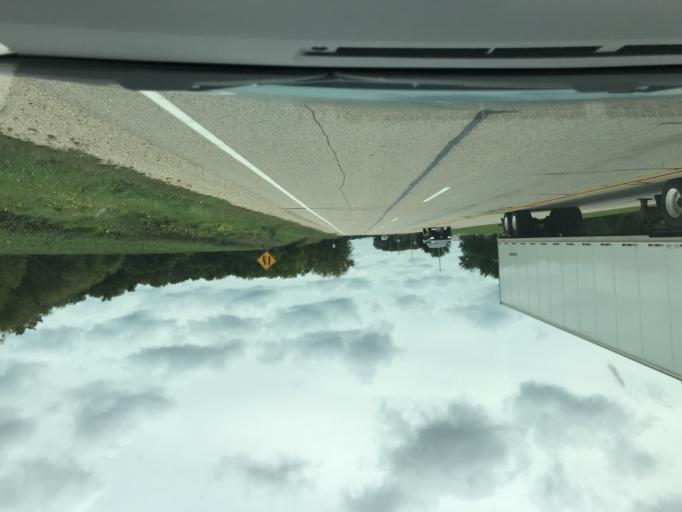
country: US
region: Wisconsin
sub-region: Racine County
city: Burlington
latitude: 42.6517
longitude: -88.2567
